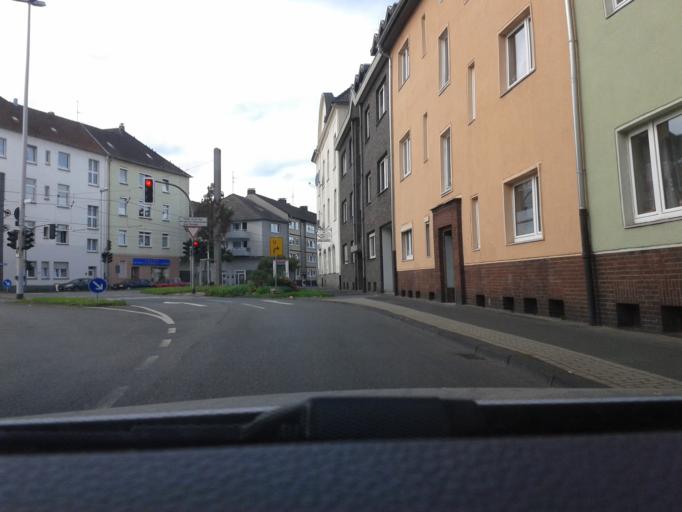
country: DE
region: North Rhine-Westphalia
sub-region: Regierungsbezirk Dusseldorf
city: Muelheim (Ruhr)
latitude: 51.4489
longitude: 6.8625
